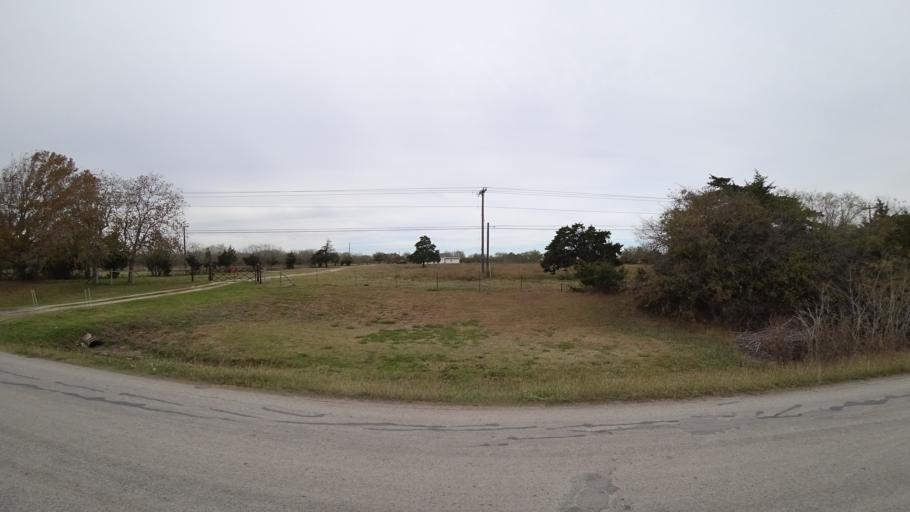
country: US
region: Texas
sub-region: Travis County
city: Garfield
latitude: 30.1066
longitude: -97.5889
